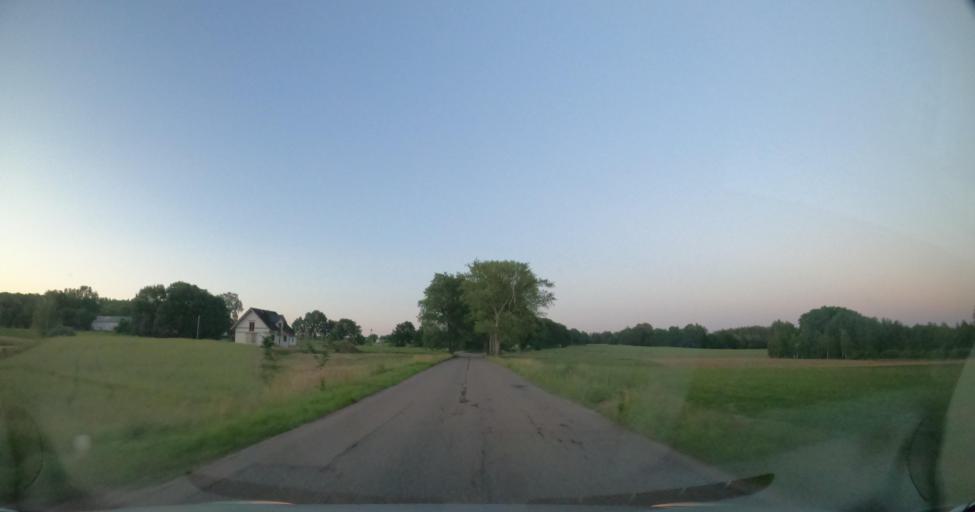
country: PL
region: Pomeranian Voivodeship
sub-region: Powiat wejherowski
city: Szemud
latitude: 54.4695
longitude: 18.1516
